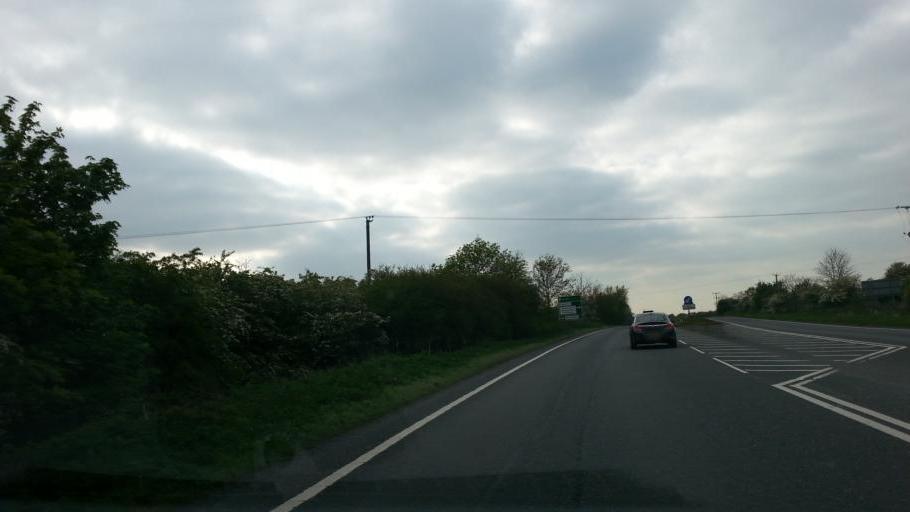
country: GB
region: England
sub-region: Nottinghamshire
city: South Collingham
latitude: 53.0730
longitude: -0.6867
